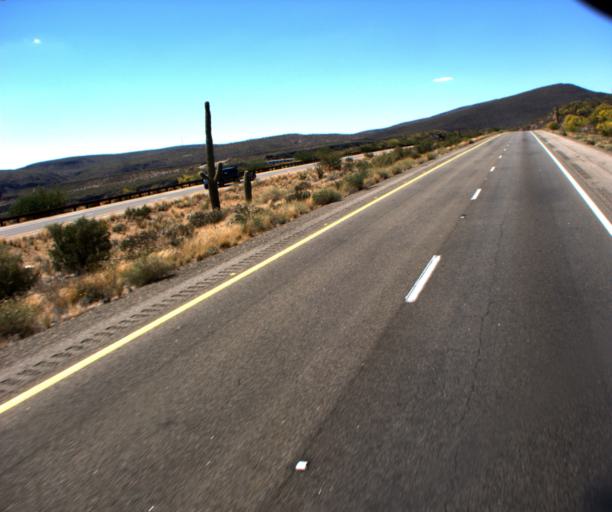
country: US
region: Arizona
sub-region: Yavapai County
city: Bagdad
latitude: 34.5379
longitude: -113.4345
